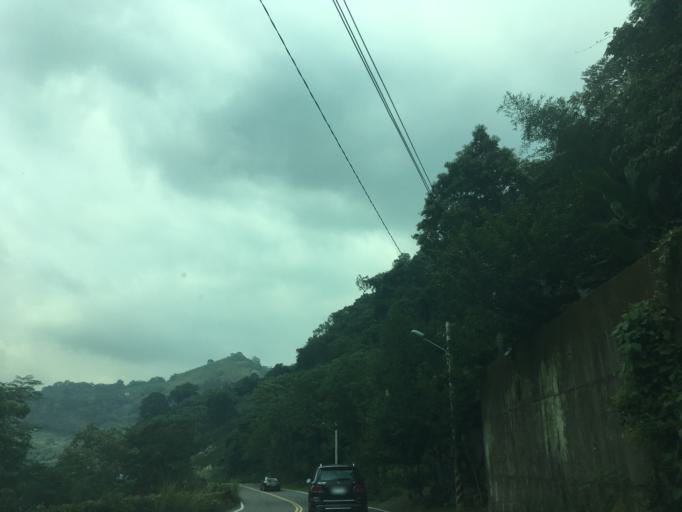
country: TW
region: Taiwan
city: Fengyuan
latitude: 24.3132
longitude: 120.9219
